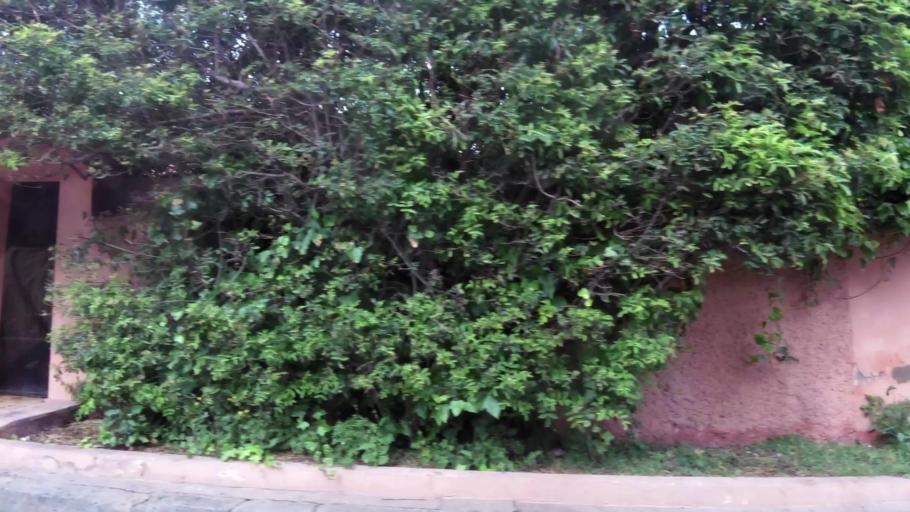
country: MA
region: Grand Casablanca
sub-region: Casablanca
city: Casablanca
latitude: 33.5938
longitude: -7.6763
